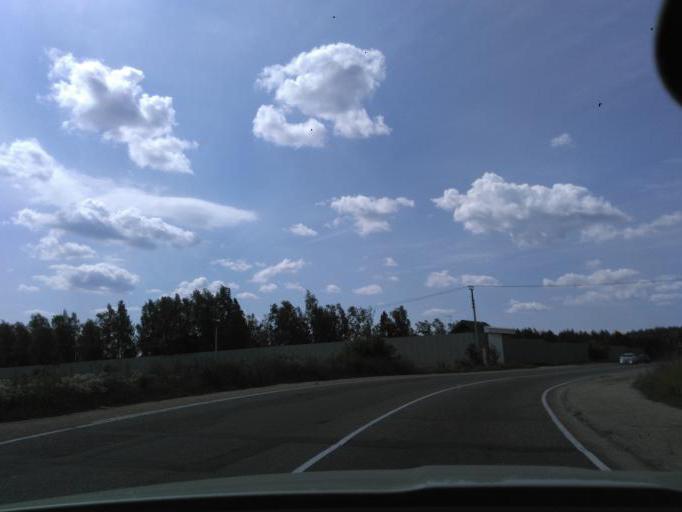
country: RU
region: Moskovskaya
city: Solnechnogorsk
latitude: 56.1677
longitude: 37.0064
